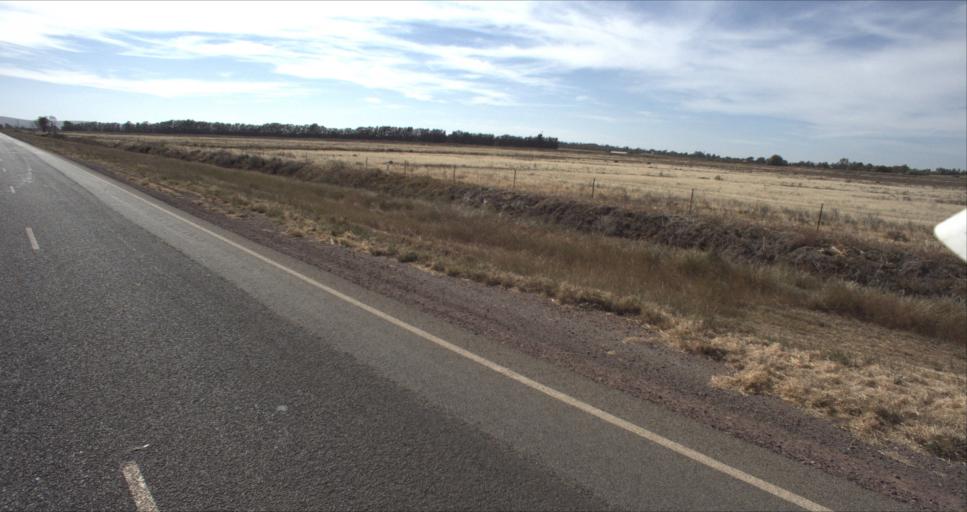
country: AU
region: New South Wales
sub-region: Leeton
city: Leeton
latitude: -34.5591
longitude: 146.4419
